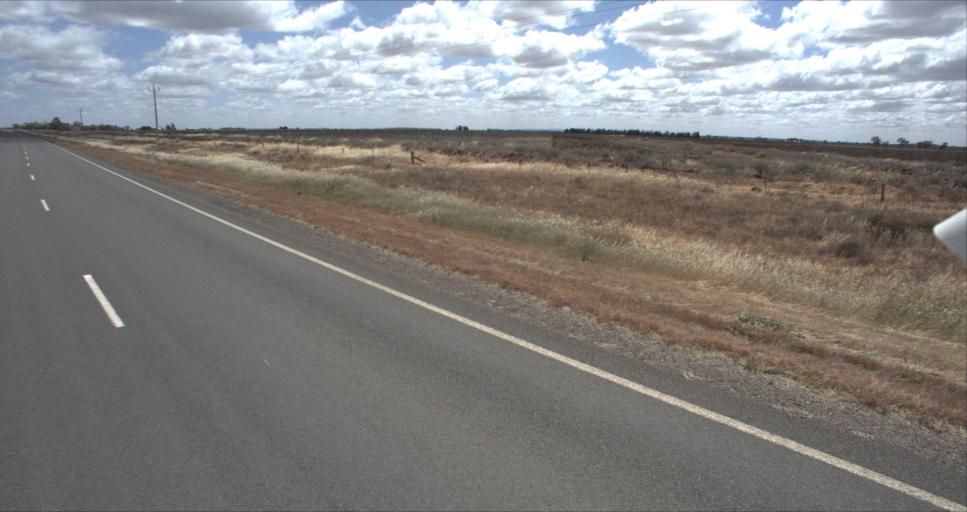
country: AU
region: New South Wales
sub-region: Murrumbidgee Shire
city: Darlington Point
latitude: -34.4936
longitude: 146.1675
